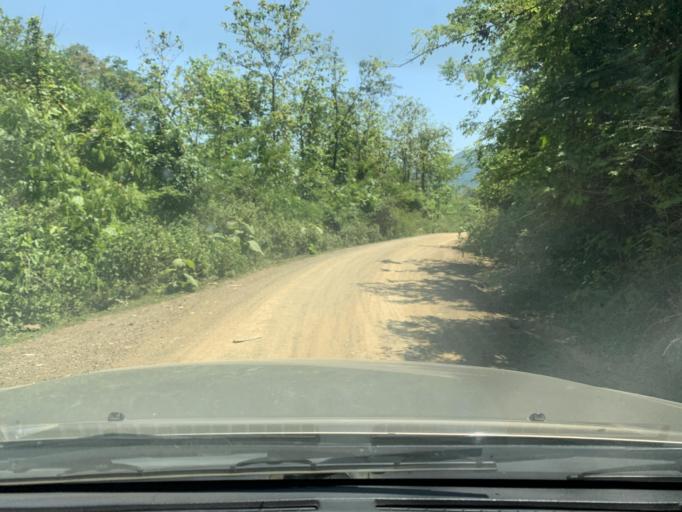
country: LA
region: Louangphabang
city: Louangphabang
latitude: 19.9053
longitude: 102.2231
